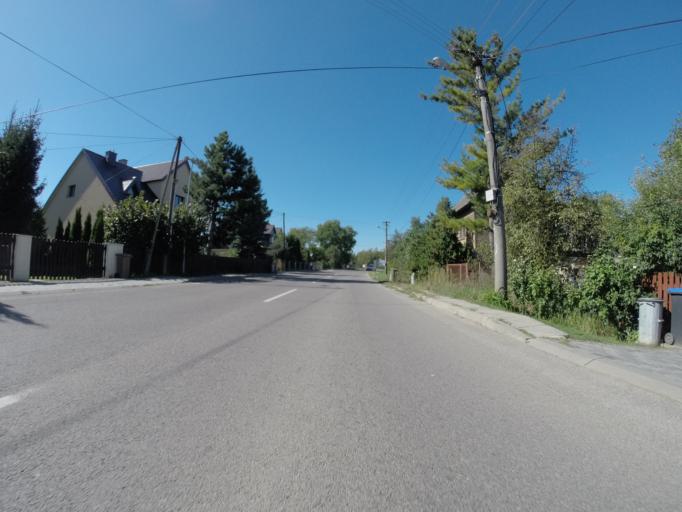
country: SK
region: Nitriansky
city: Puchov
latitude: 49.0685
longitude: 18.3359
